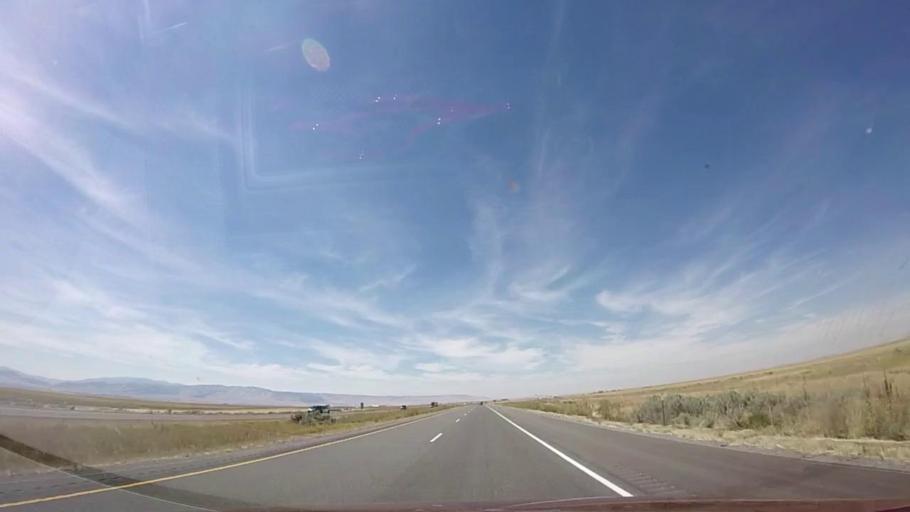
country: US
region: Idaho
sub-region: Minidoka County
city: Rupert
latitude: 42.3180
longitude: -113.1989
